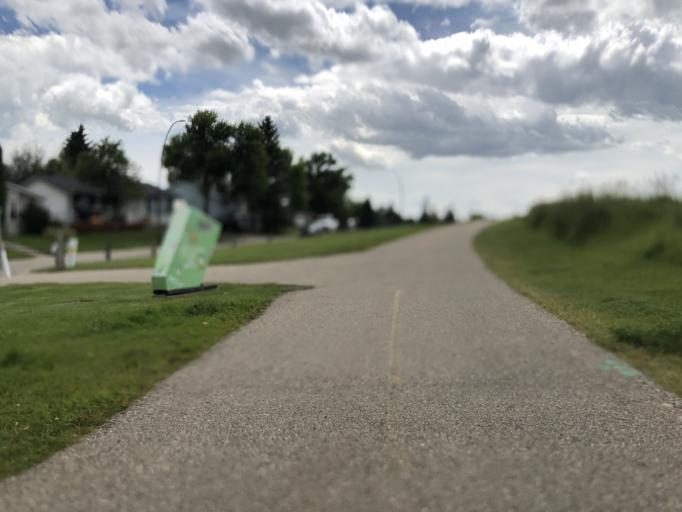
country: CA
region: Alberta
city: Calgary
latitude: 50.9935
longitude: -114.0217
